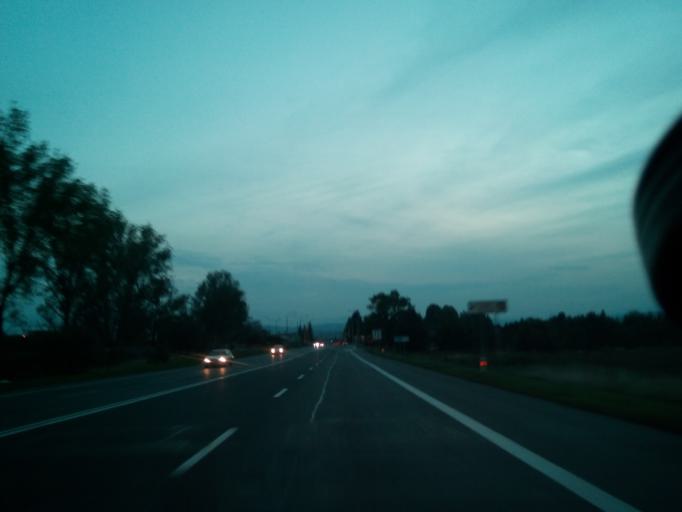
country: SK
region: Presovsky
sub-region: Okres Presov
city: Presov
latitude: 49.0263
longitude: 21.2890
